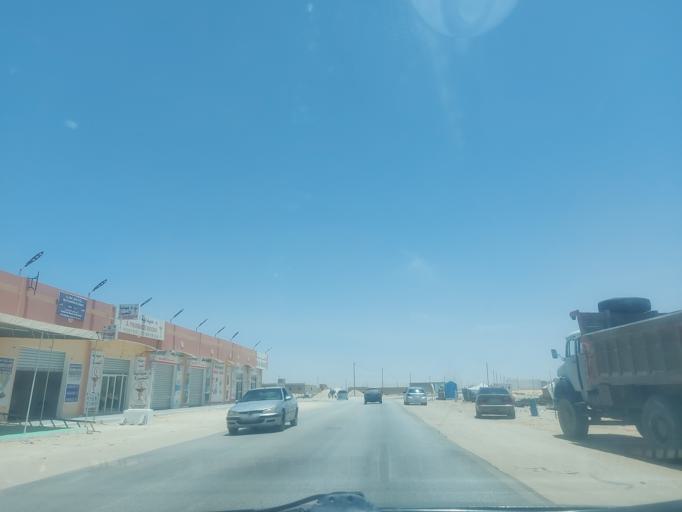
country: MR
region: Nouakchott
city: Nouakchott
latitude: 18.0853
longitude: -15.9520
